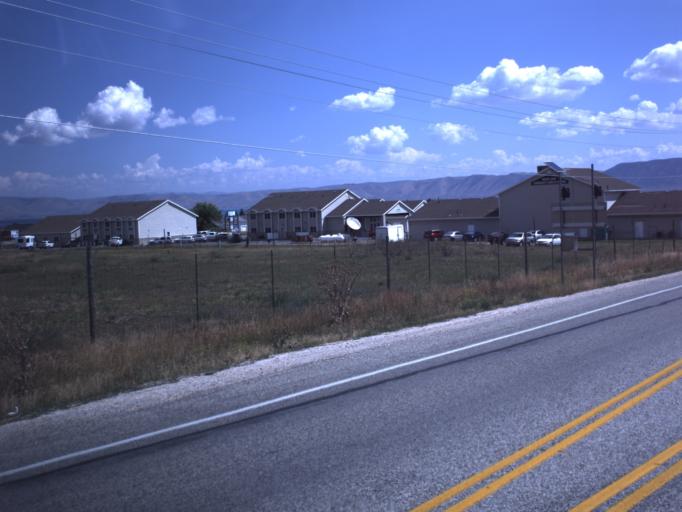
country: US
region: Idaho
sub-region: Bear Lake County
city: Paris
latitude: 41.9467
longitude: -111.4026
